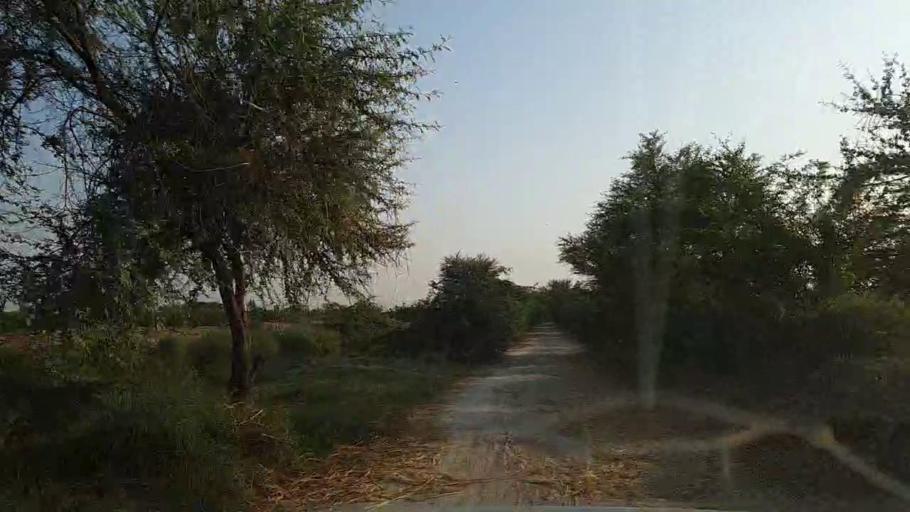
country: PK
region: Sindh
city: Daro Mehar
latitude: 24.7705
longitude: 68.1935
